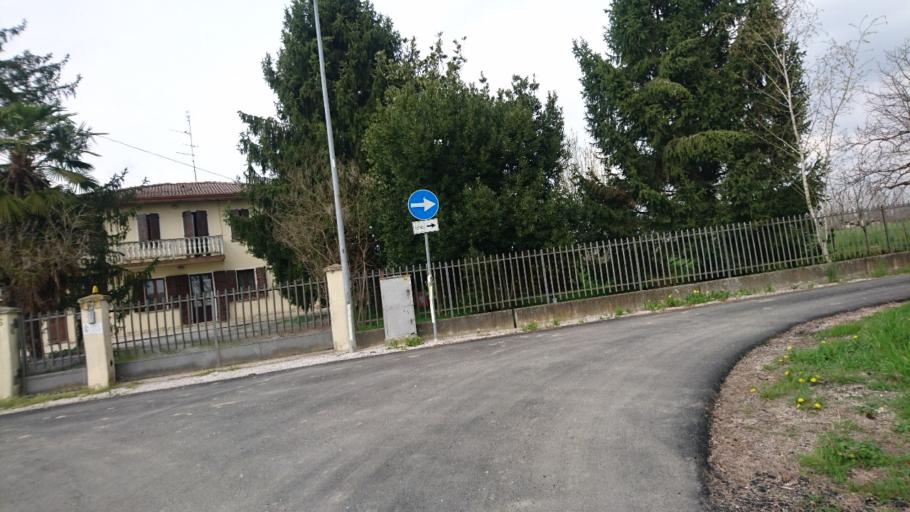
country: IT
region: Veneto
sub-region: Provincia di Padova
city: Villafranca Padovana
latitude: 45.4959
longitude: 11.8207
